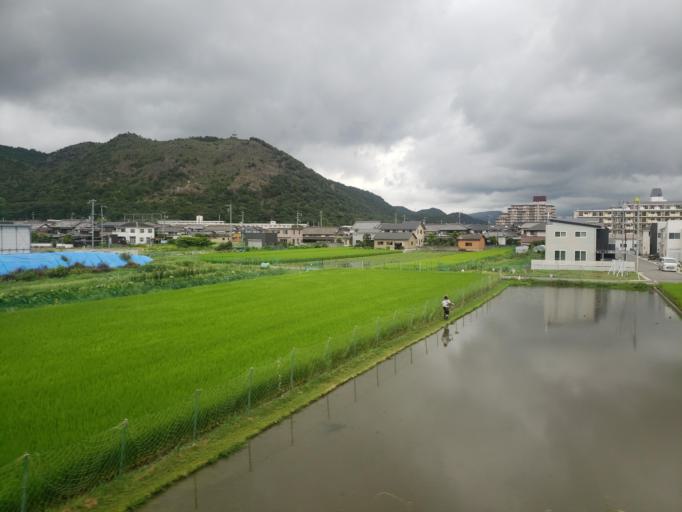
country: JP
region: Hyogo
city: Himeji
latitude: 34.8108
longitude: 134.6310
